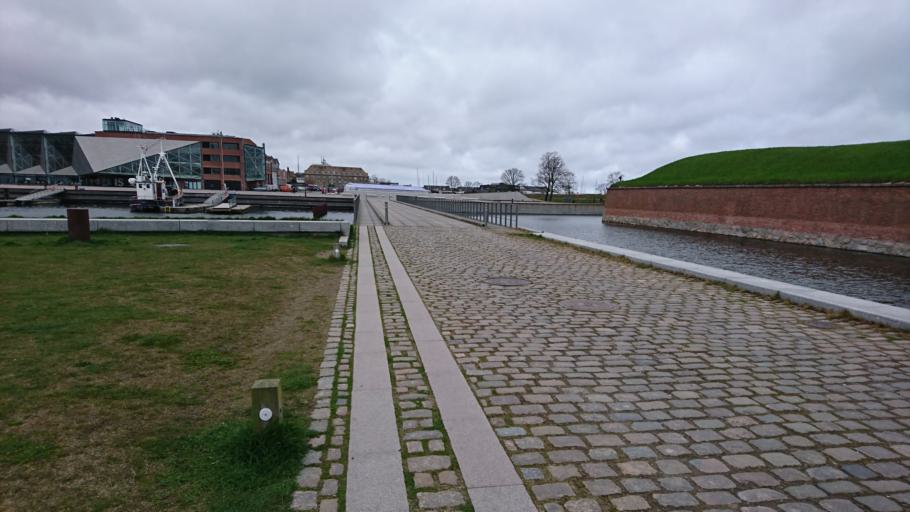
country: DK
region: Capital Region
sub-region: Helsingor Kommune
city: Helsingor
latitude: 56.0379
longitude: 12.6185
